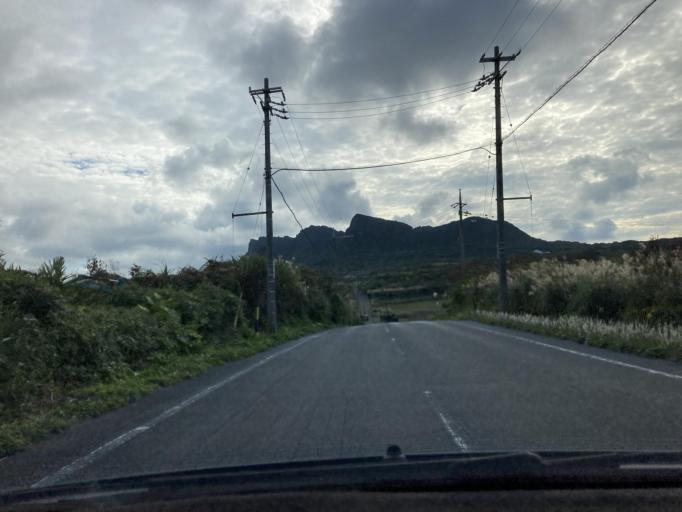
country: JP
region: Okinawa
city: Nago
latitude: 26.8684
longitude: 128.2609
